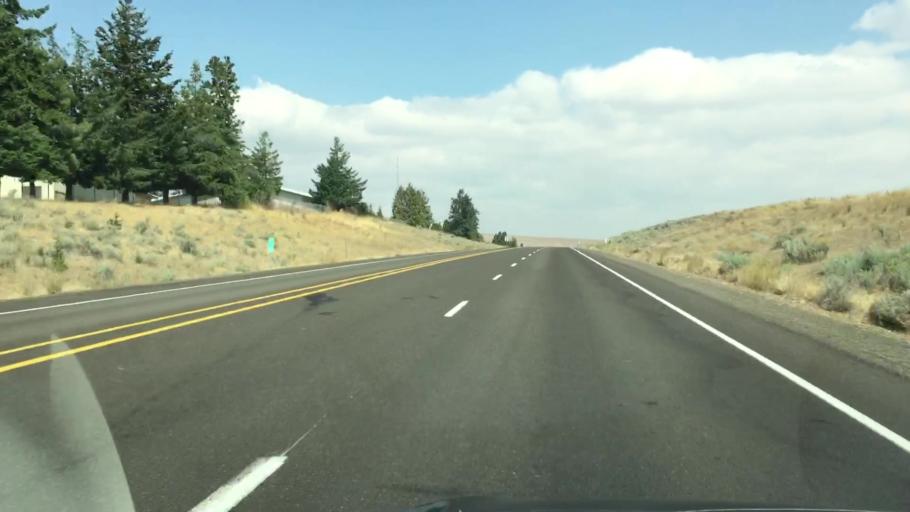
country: US
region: Oregon
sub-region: Wasco County
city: The Dalles
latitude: 45.4548
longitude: -121.1219
